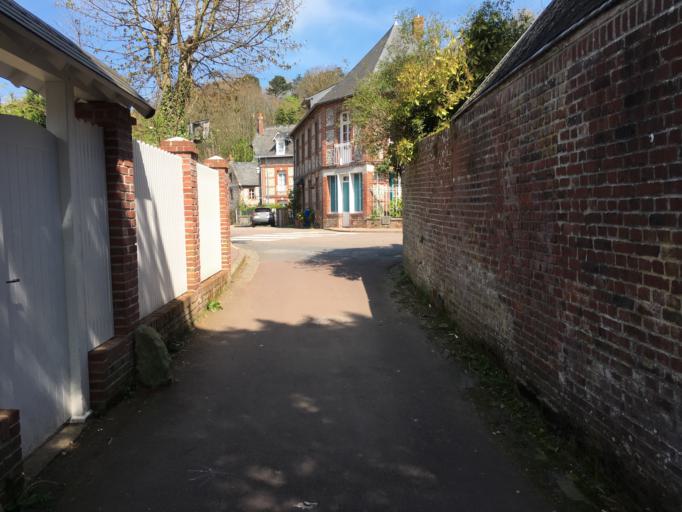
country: FR
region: Haute-Normandie
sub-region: Departement de la Seine-Maritime
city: Saint-Valery-en-Caux
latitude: 49.8710
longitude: 0.8007
